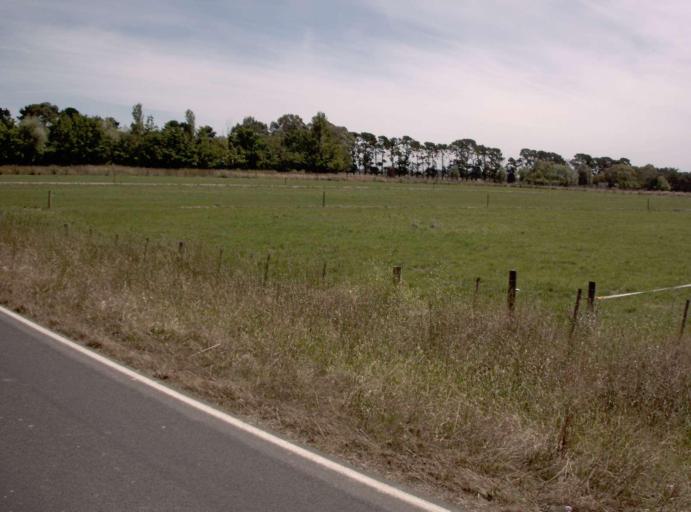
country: AU
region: Victoria
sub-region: Wellington
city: Heyfield
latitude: -38.0705
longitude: 146.8707
